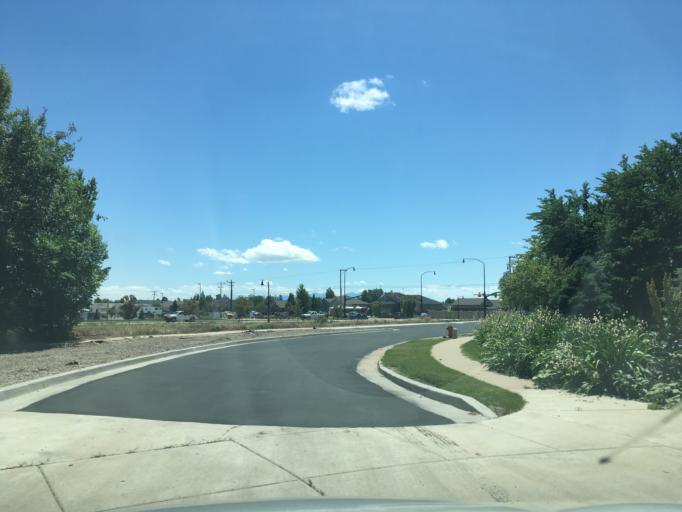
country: US
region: Utah
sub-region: Davis County
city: Layton
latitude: 41.0540
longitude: -111.9706
